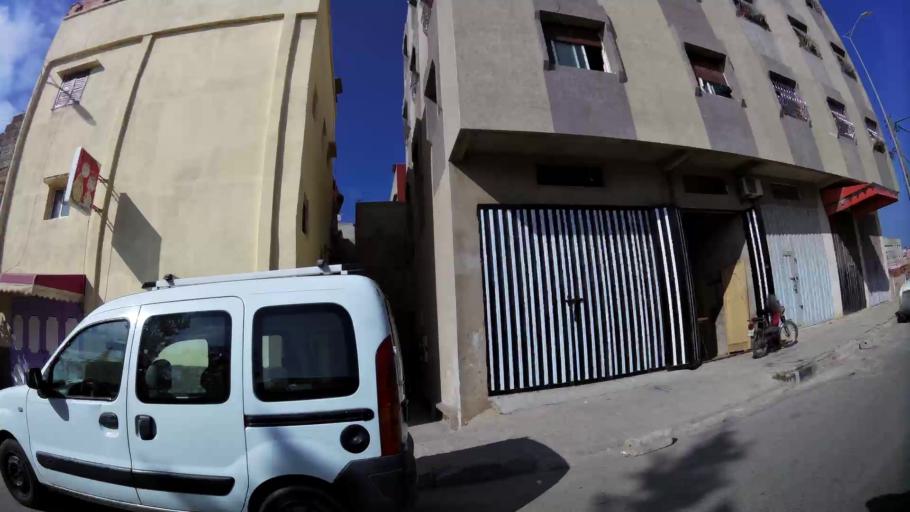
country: MA
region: Rabat-Sale-Zemmour-Zaer
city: Sale
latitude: 34.0613
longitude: -6.7704
